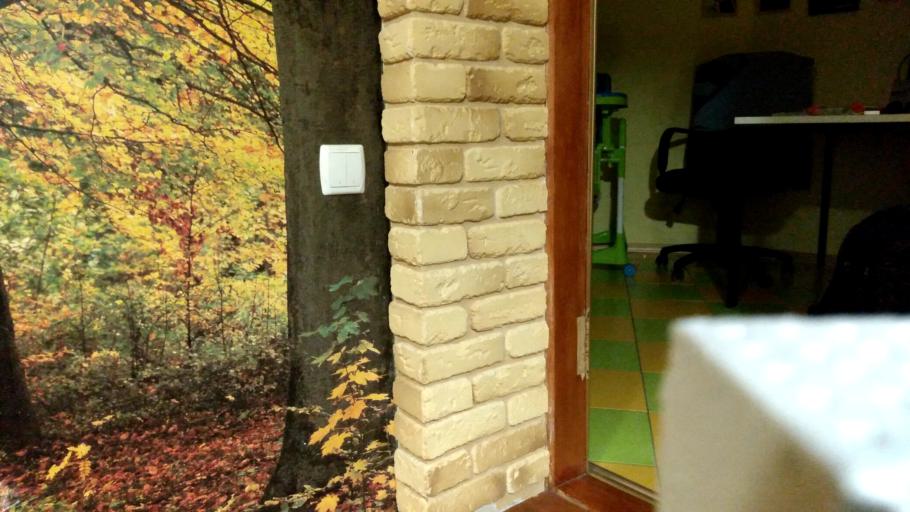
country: RU
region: Arkhangelskaya
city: Kargopol'
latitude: 61.5918
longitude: 37.7470
